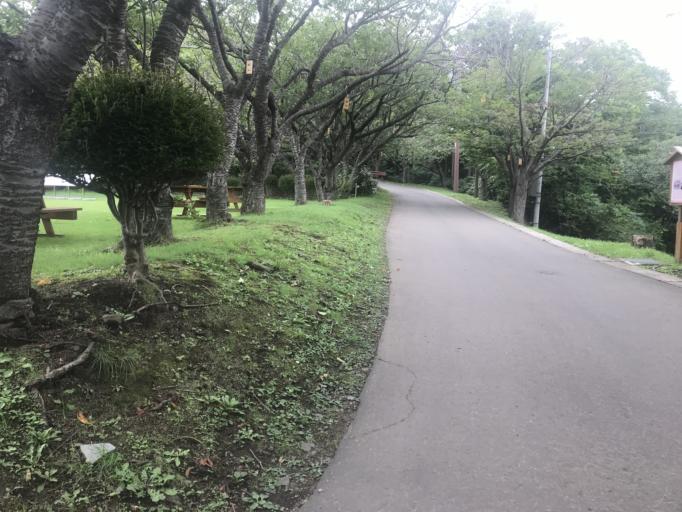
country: JP
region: Hokkaido
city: Kamiiso
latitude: 41.4324
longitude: 140.1091
